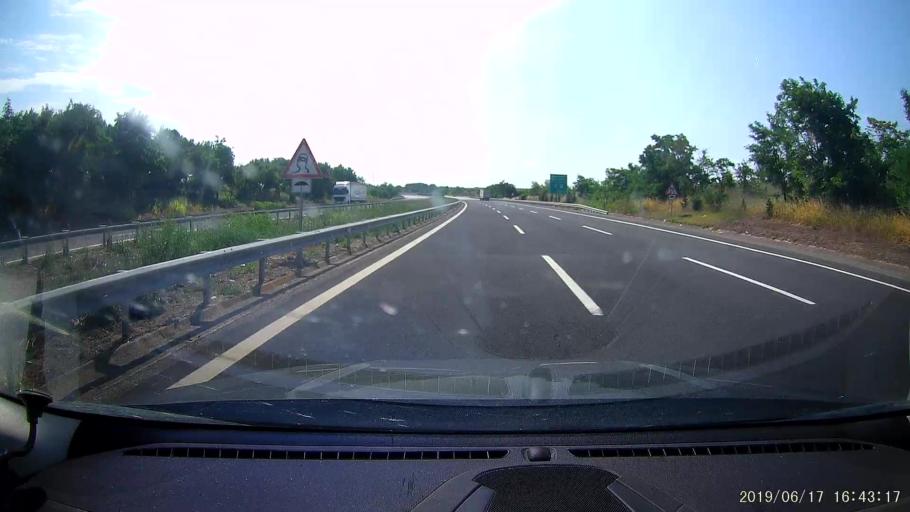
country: TR
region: Kirklareli
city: Luleburgaz
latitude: 41.4803
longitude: 27.2977
